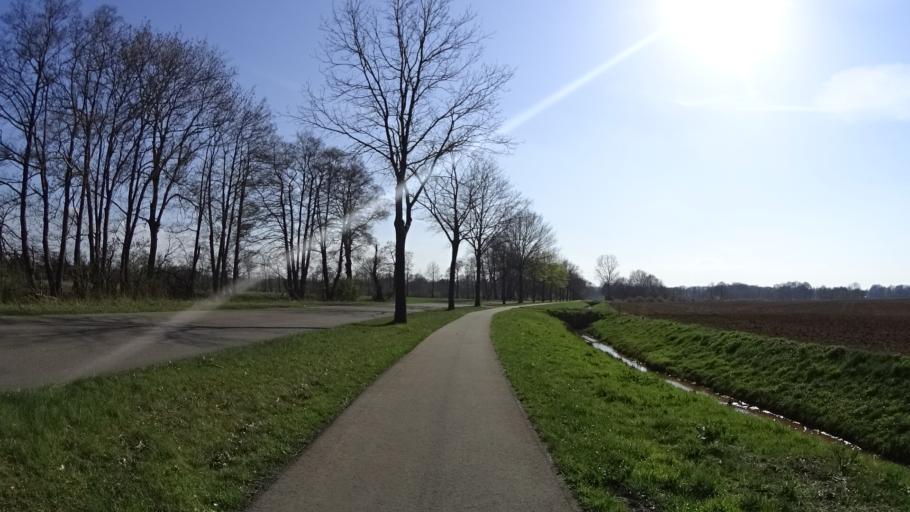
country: DE
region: Lower Saxony
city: Walchum
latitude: 52.9328
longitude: 7.3116
